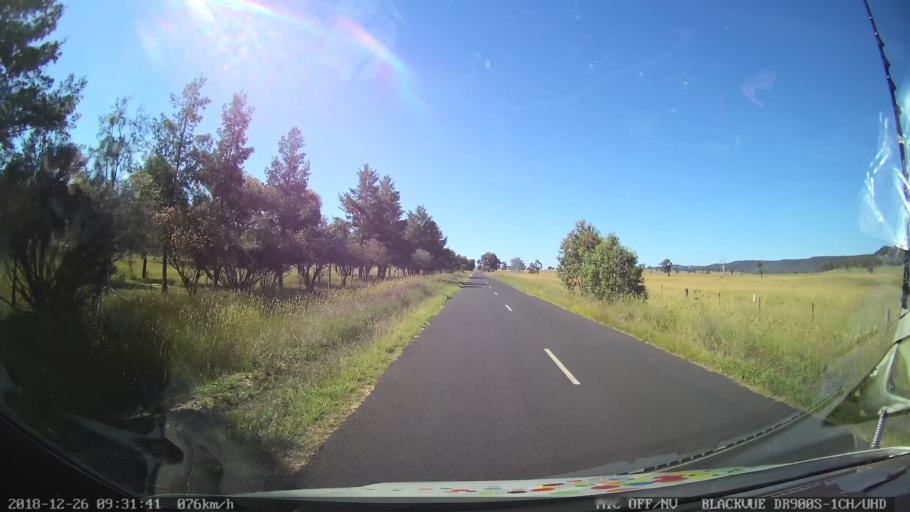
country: AU
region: New South Wales
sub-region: Mid-Western Regional
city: Kandos
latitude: -32.8756
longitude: 150.0320
